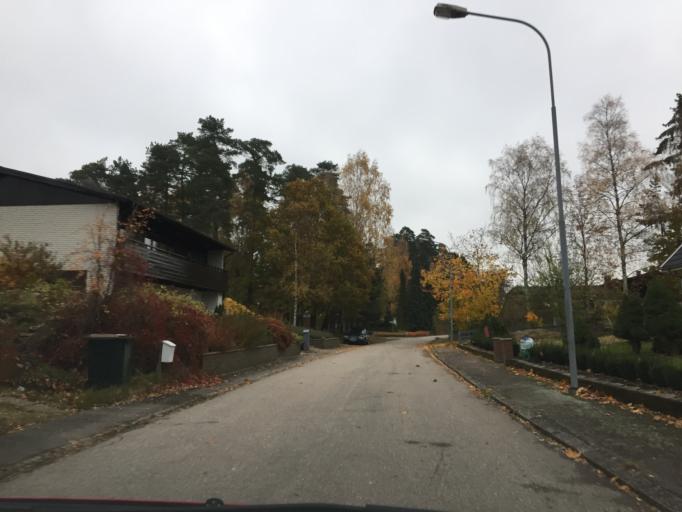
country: SE
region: Vaestra Goetaland
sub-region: Trollhattan
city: Trollhattan
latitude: 58.2619
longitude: 12.2790
